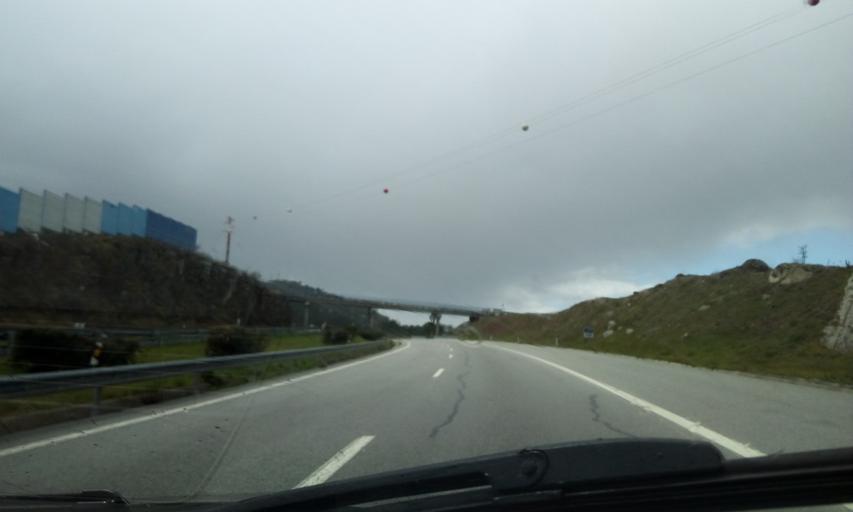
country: PT
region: Viseu
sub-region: Mangualde
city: Mangualde
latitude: 40.6162
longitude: -7.7192
